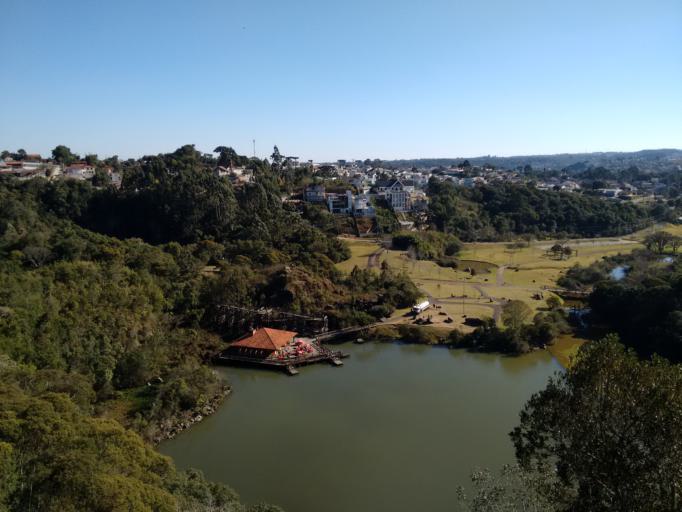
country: BR
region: Parana
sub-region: Curitiba
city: Curitiba
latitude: -25.3792
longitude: -49.2834
